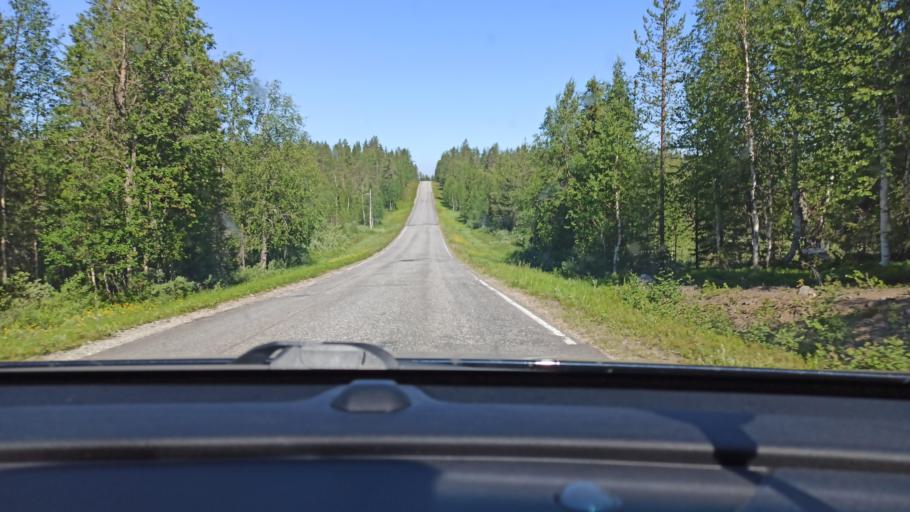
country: FI
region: Lapland
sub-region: Tunturi-Lappi
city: Kolari
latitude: 67.6770
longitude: 24.1425
